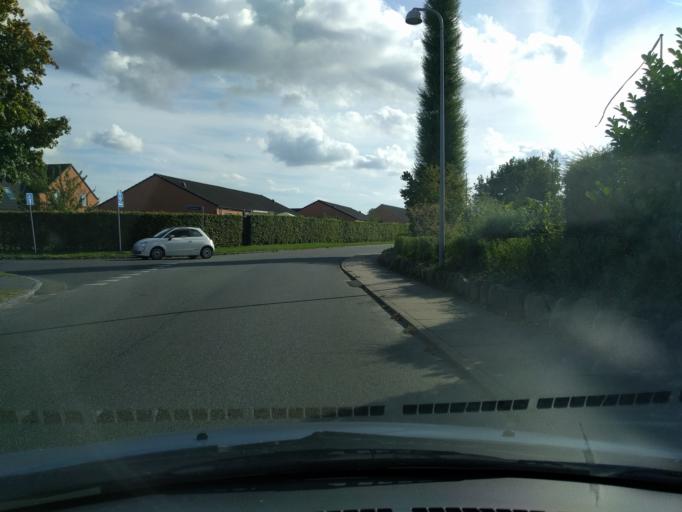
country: DK
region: South Denmark
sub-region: Odense Kommune
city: Neder Holluf
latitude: 55.3578
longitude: 10.5002
